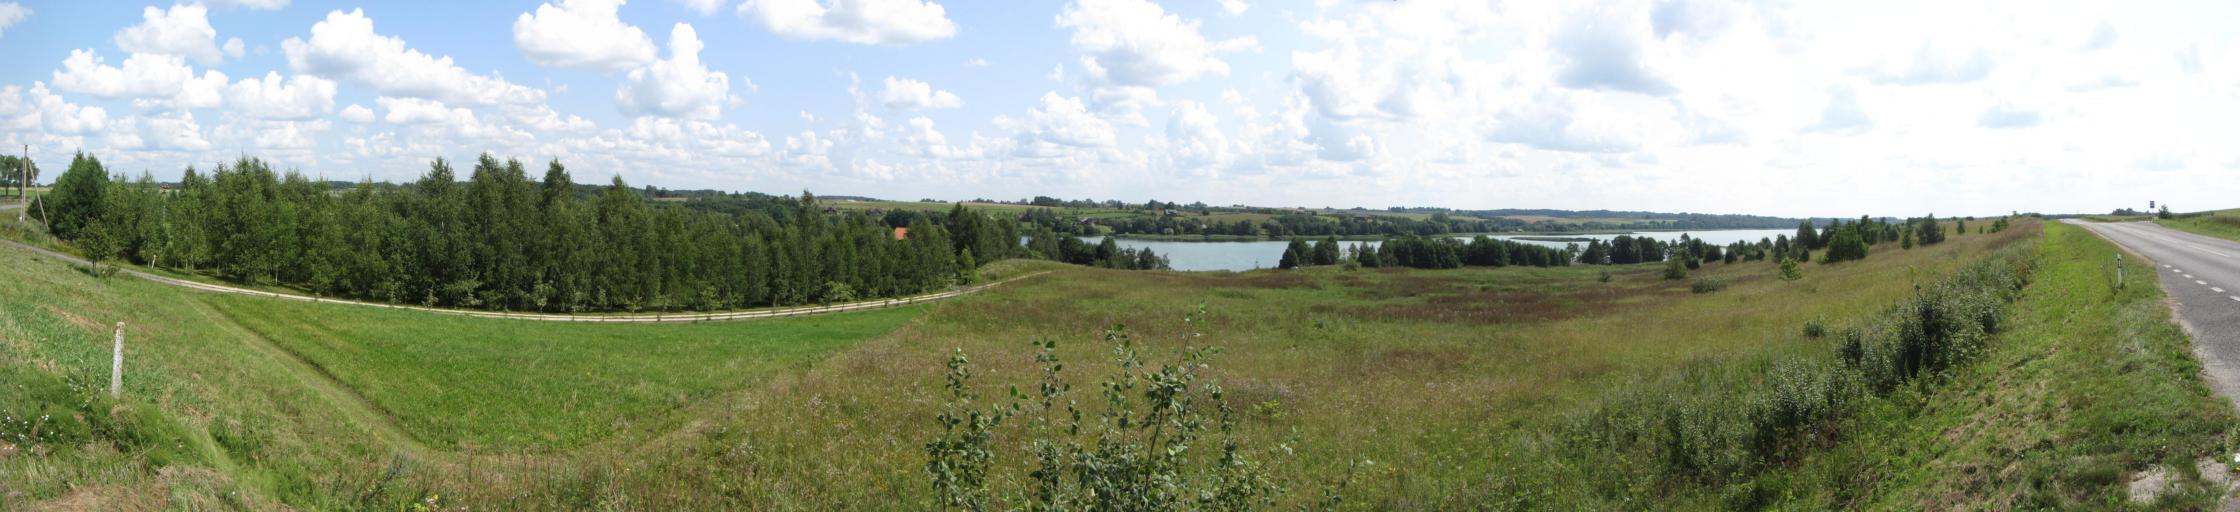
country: LT
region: Vilnius County
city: Ukmerge
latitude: 55.1370
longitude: 24.7464
